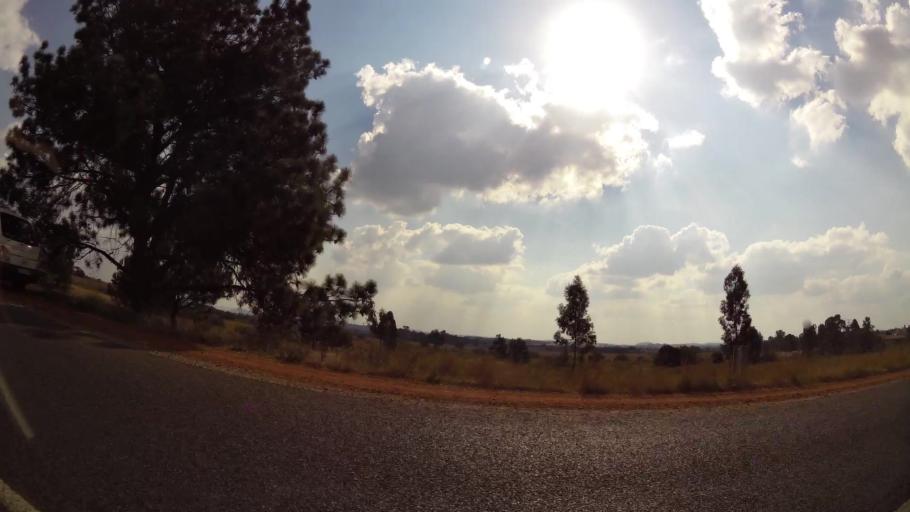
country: ZA
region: Gauteng
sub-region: City of Tshwane Metropolitan Municipality
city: Centurion
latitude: -25.8640
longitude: 28.2389
